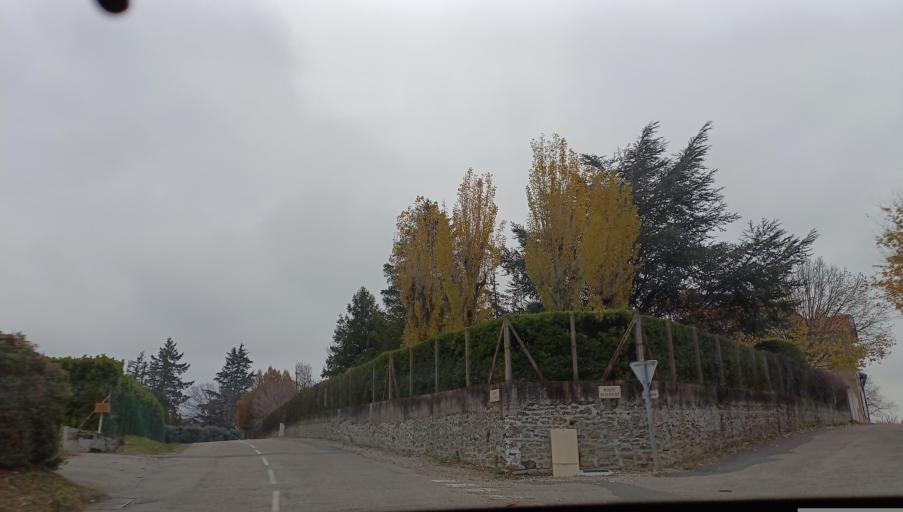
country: FR
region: Rhone-Alpes
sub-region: Departement de l'Isere
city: Serpaize
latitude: 45.5560
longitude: 4.9247
